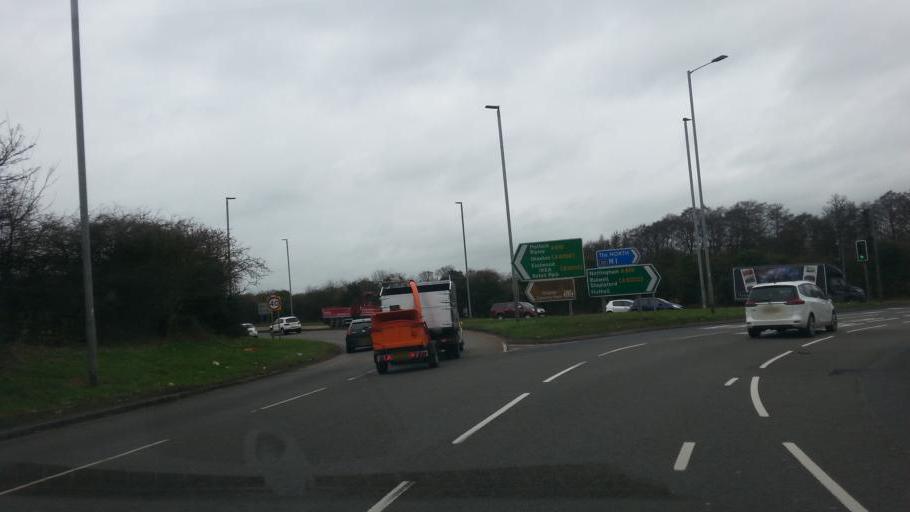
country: GB
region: England
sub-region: Nottinghamshire
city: Kimberley
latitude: 52.9898
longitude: -1.2356
